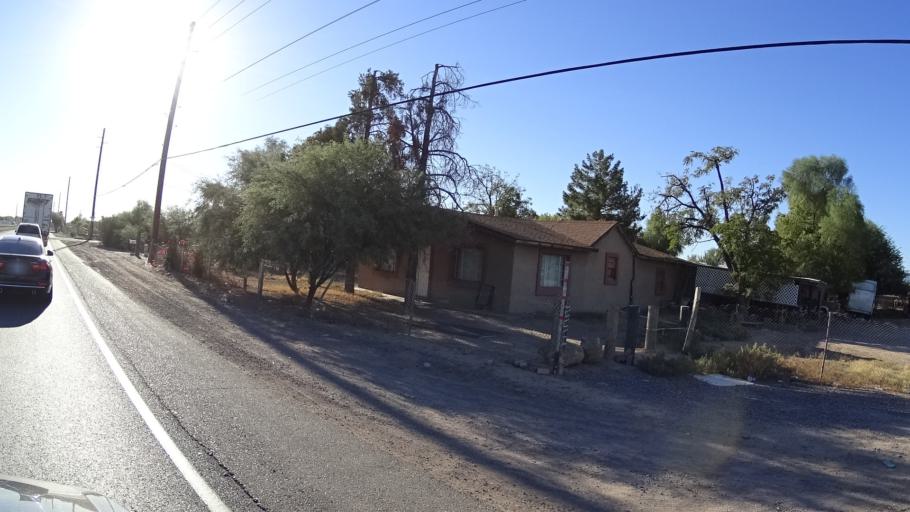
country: US
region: Arizona
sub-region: Maricopa County
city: Tolleson
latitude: 33.4228
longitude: -112.2093
